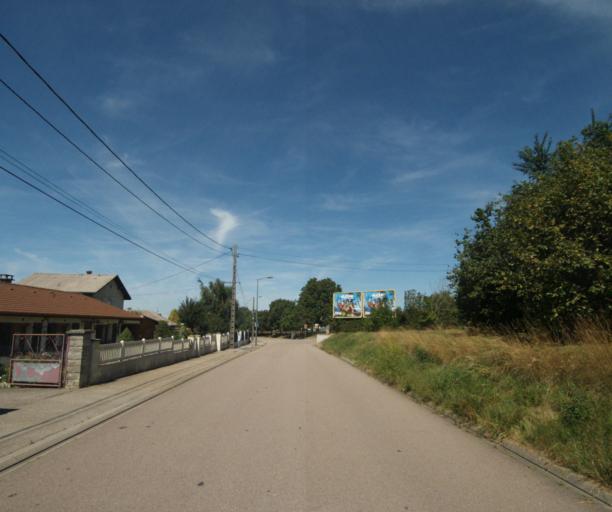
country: FR
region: Lorraine
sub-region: Departement des Vosges
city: Golbey
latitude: 48.1977
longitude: 6.4514
